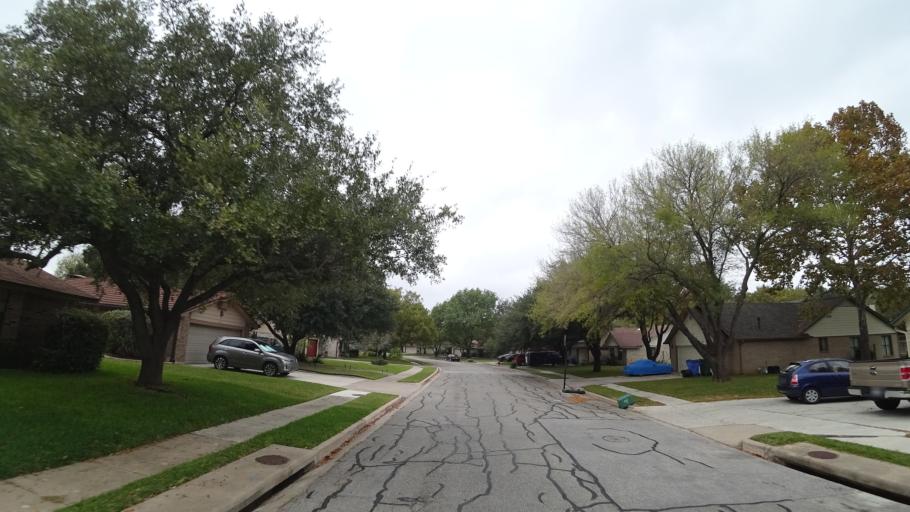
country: US
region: Texas
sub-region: Travis County
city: Pflugerville
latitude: 30.4419
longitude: -97.6145
